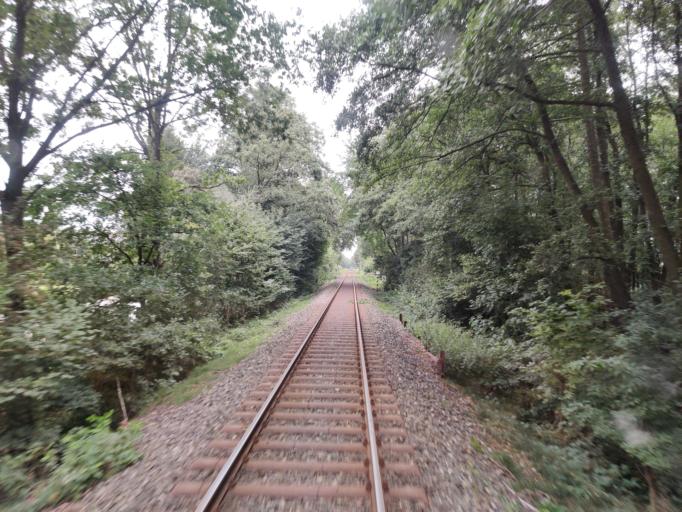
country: DE
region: Lower Saxony
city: Deinste
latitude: 53.5292
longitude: 9.4398
